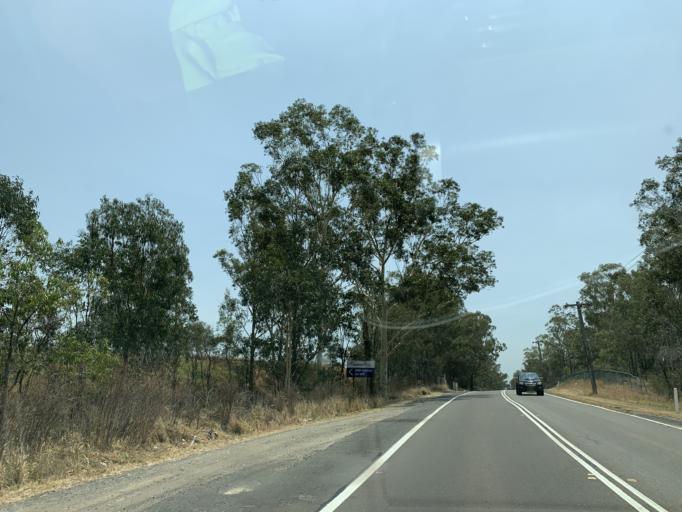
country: AU
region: New South Wales
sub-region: Fairfield
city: Horsley Park
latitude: -33.8299
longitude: 150.8730
